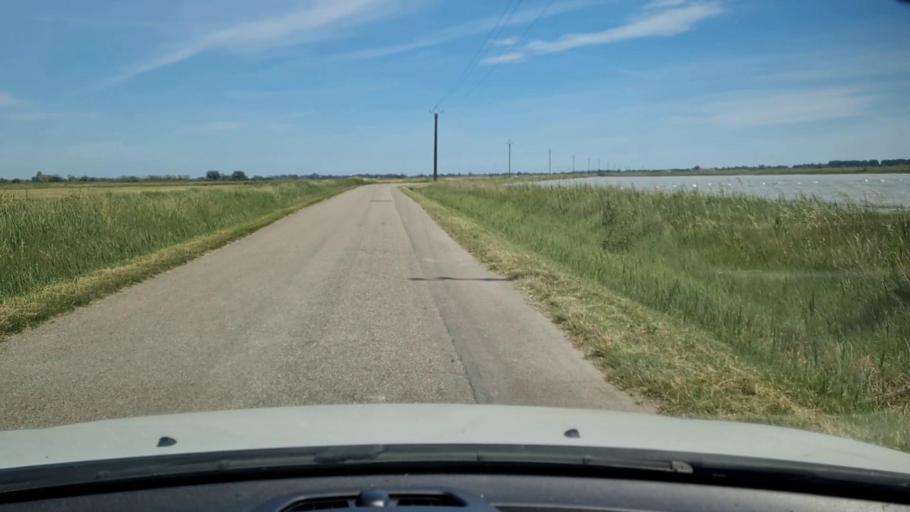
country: FR
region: Languedoc-Roussillon
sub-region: Departement du Gard
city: Saint-Gilles
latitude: 43.6091
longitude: 4.4294
